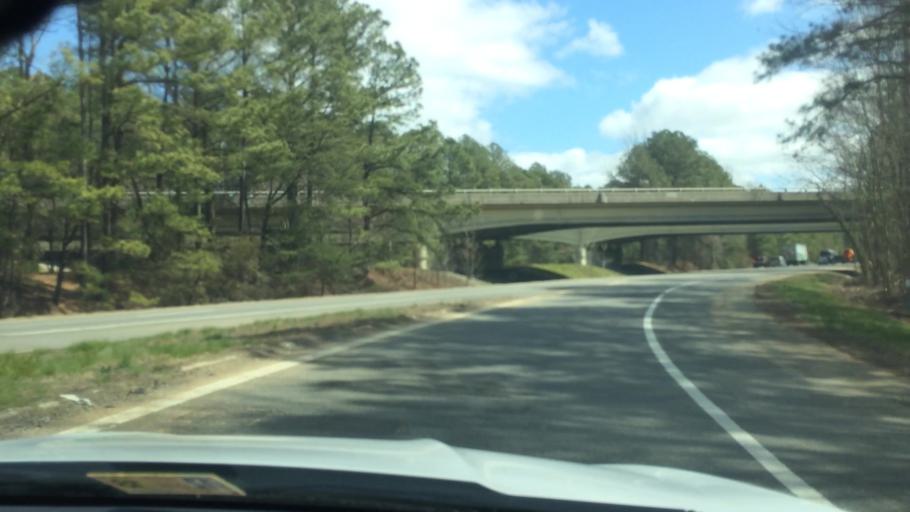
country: US
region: Virginia
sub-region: King William County
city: West Point
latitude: 37.4211
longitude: -76.8253
